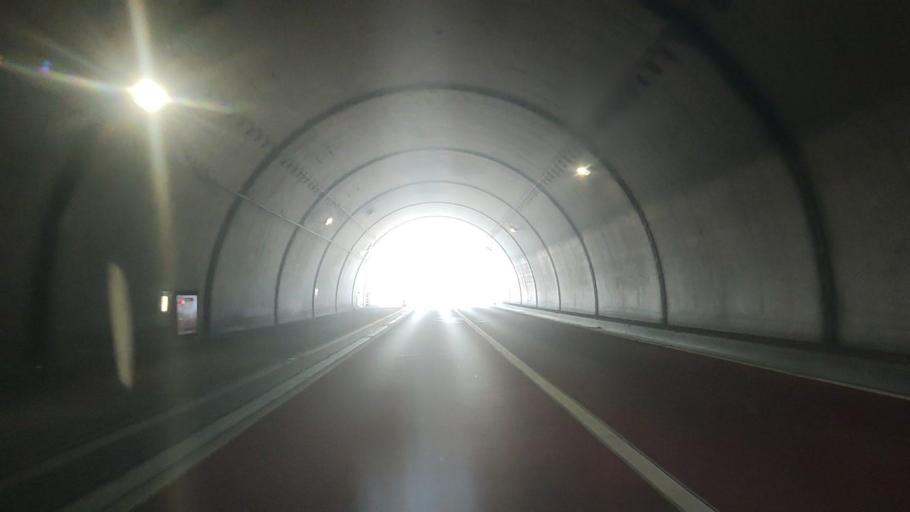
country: JP
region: Oita
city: Oita
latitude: 33.0947
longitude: 131.6506
